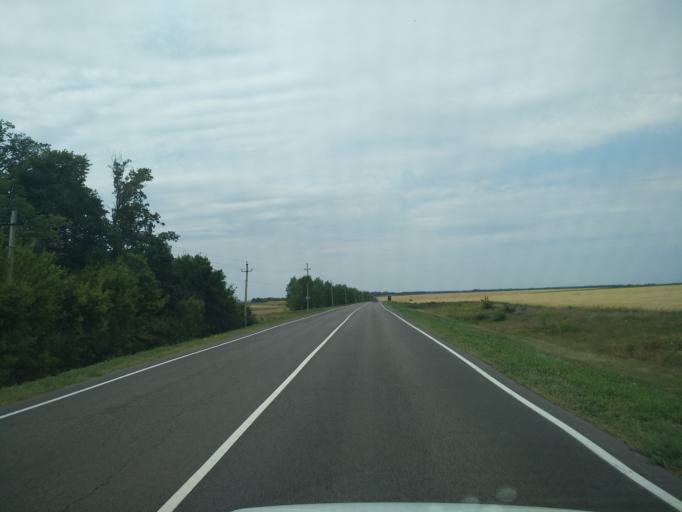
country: RU
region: Voronezj
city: Pereleshinskiy
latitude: 51.8250
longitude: 40.2784
